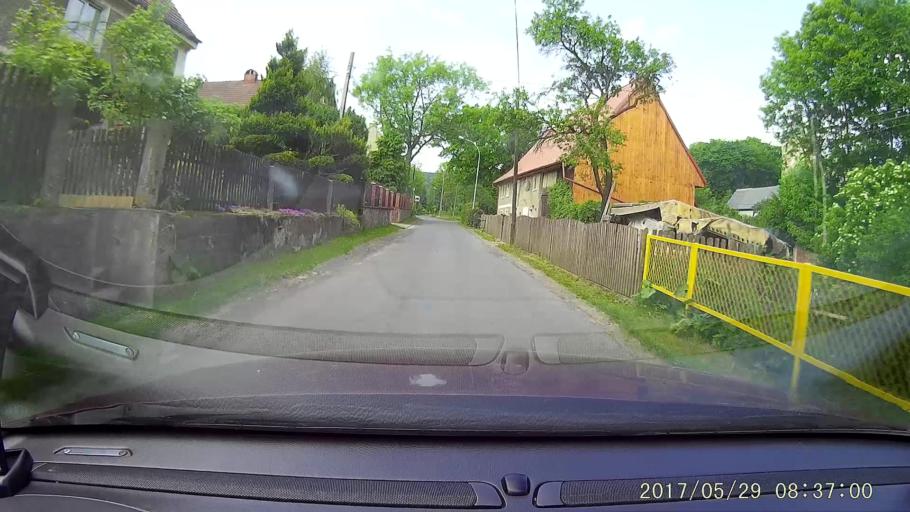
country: PL
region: Lower Silesian Voivodeship
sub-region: Powiat zlotoryjski
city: Swierzawa
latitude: 50.9953
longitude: 15.8525
